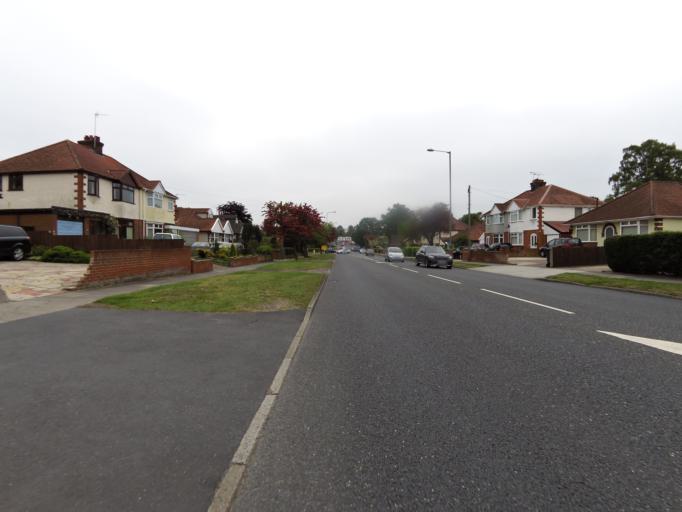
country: GB
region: England
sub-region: Suffolk
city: Kesgrave
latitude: 52.0443
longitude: 1.1995
